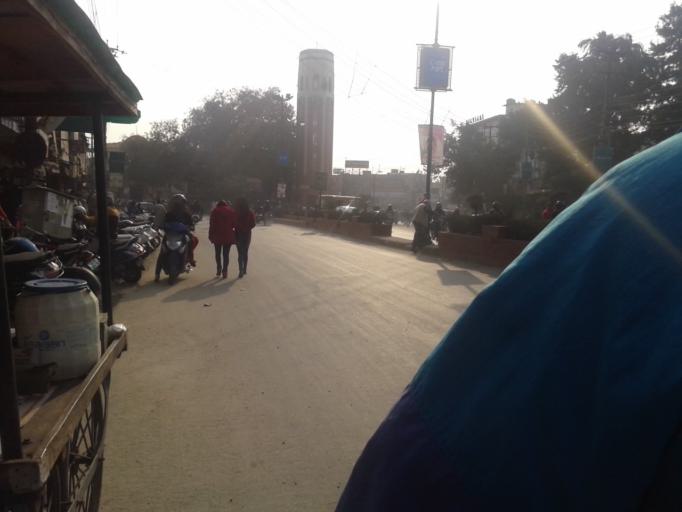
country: IN
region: Uttarakhand
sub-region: Dehradun
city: Dehradun
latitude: 30.3293
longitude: 78.0444
